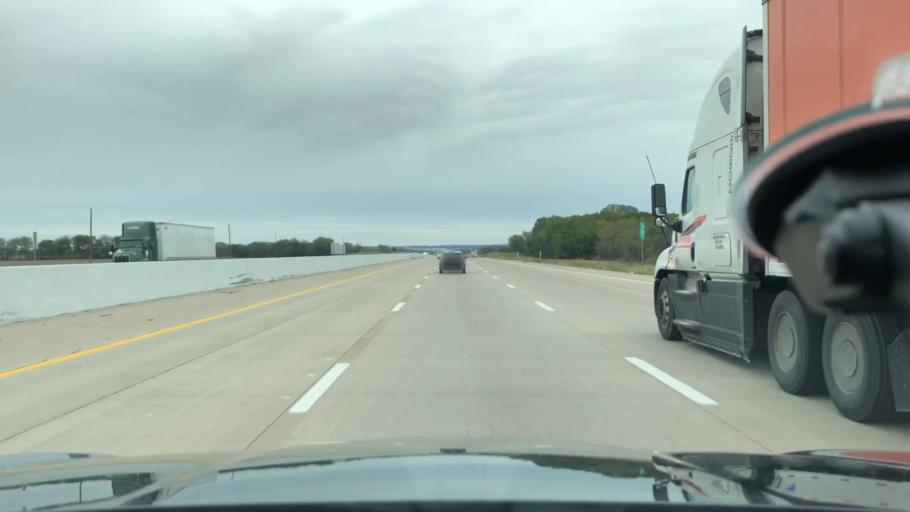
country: US
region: Texas
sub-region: Ellis County
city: Italy
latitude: 32.2037
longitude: -96.8953
